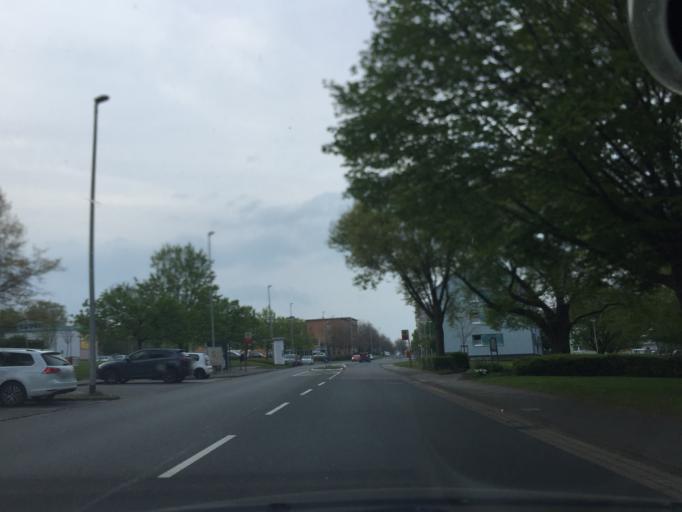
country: DE
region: Lower Saxony
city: Hildesheim
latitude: 52.1449
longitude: 9.9220
